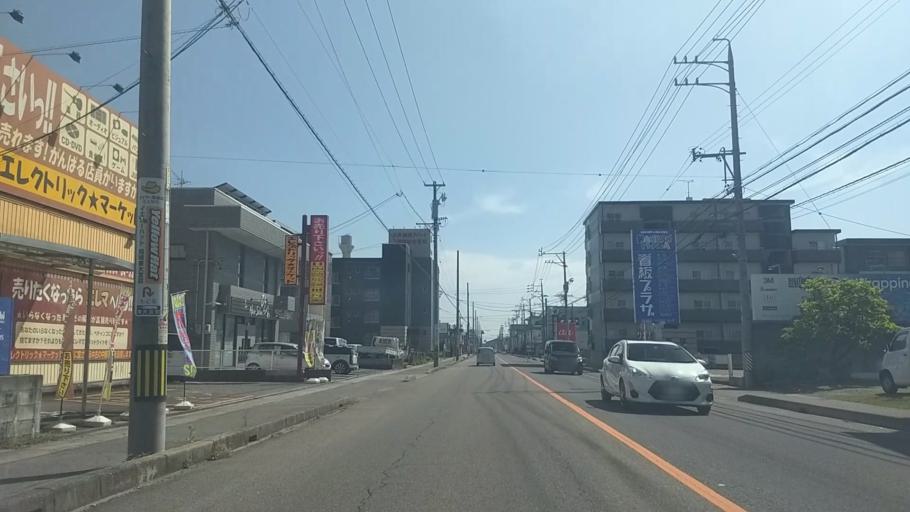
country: JP
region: Aichi
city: Okazaki
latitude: 34.9748
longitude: 137.1351
